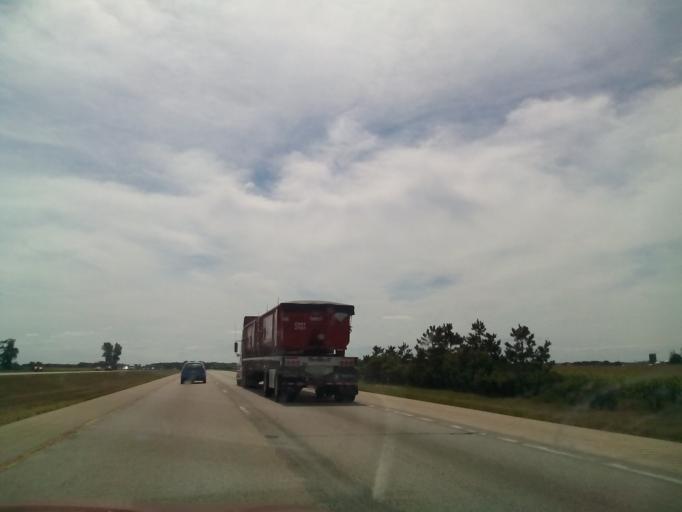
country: US
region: Illinois
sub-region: Ogle County
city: Davis Junction
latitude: 42.0766
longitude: -89.0228
